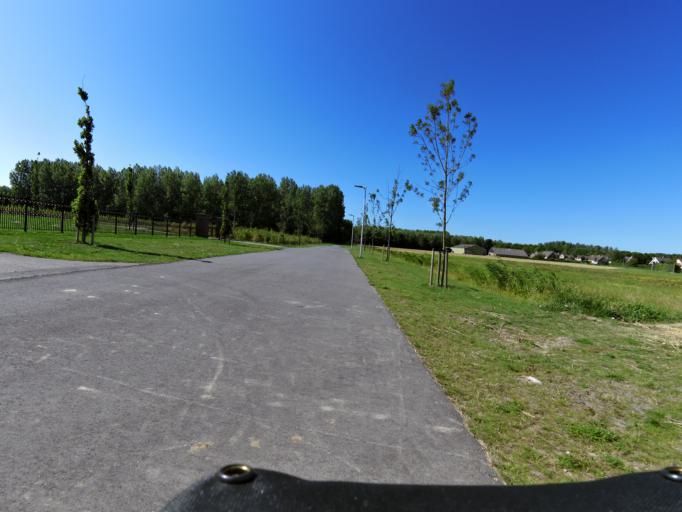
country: NL
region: South Holland
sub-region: Gemeente Goeree-Overflakkee
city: Goedereede
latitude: 51.8016
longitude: 4.0205
